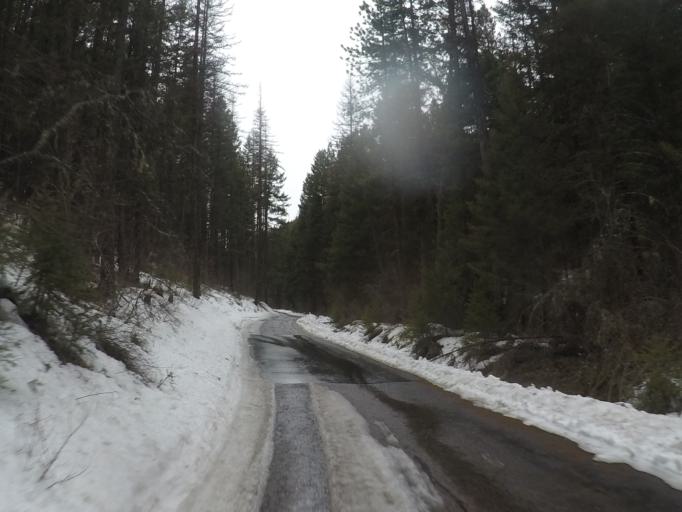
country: US
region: Montana
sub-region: Missoula County
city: Missoula
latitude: 46.9292
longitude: -113.9680
